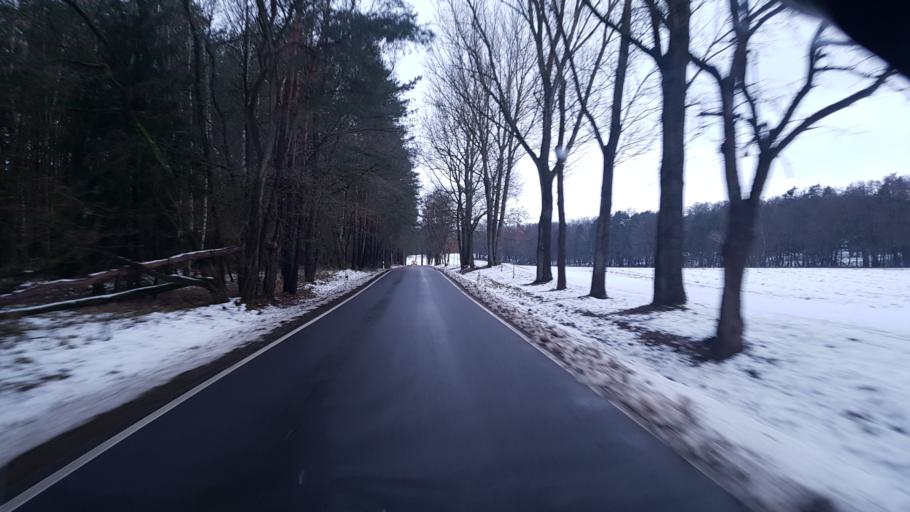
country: DE
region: Brandenburg
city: Gross Lindow
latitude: 52.2797
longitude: 14.5267
